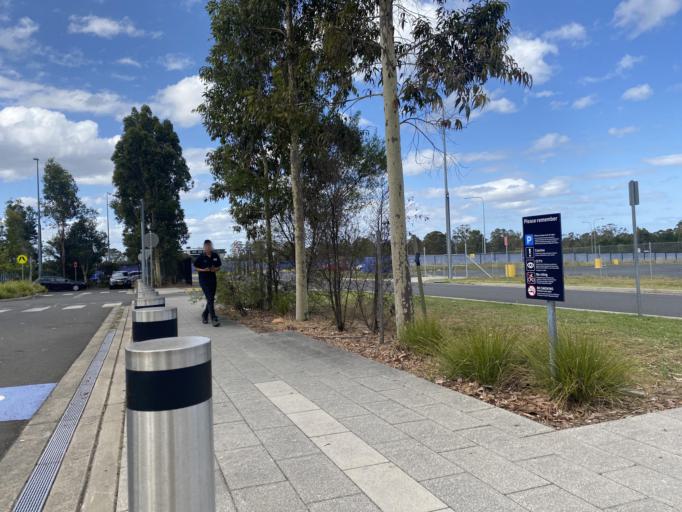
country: AU
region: New South Wales
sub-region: Campbelltown Municipality
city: Denham Court
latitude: -33.9688
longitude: 150.8586
